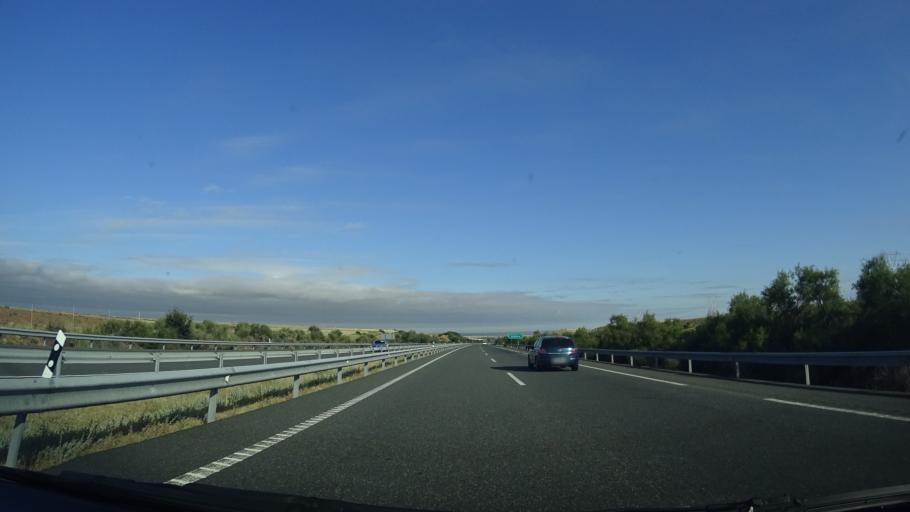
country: ES
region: Castille and Leon
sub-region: Provincia de Segovia
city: Labajos
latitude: 40.8262
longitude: -4.5172
